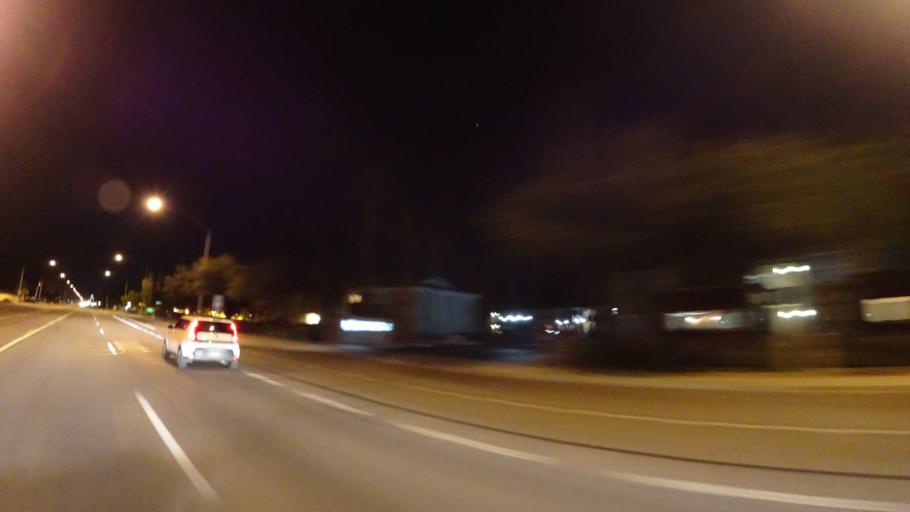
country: US
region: Arizona
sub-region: Maricopa County
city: Gilbert
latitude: 33.3938
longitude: -111.7345
